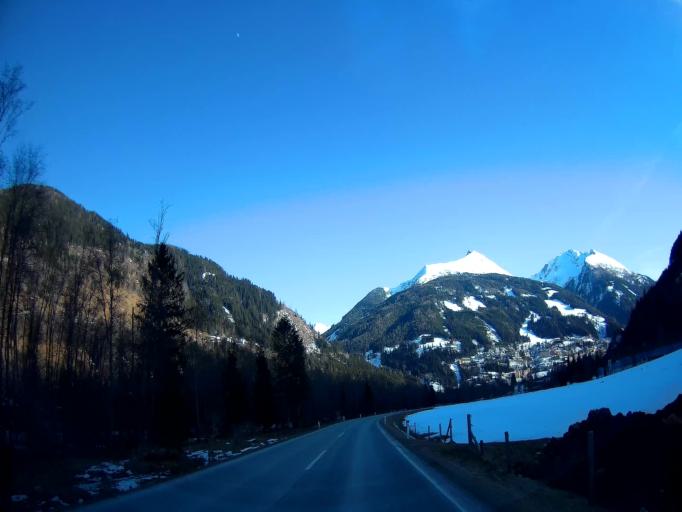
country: AT
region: Salzburg
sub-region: Politischer Bezirk Sankt Johann im Pongau
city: Bad Gastein
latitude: 47.1380
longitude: 13.1281
